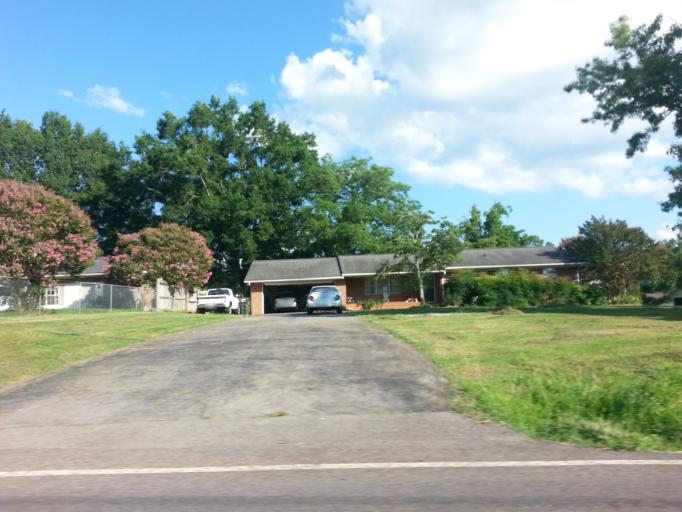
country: US
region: Tennessee
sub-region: Blount County
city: Maryville
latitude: 35.7056
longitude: -84.0178
